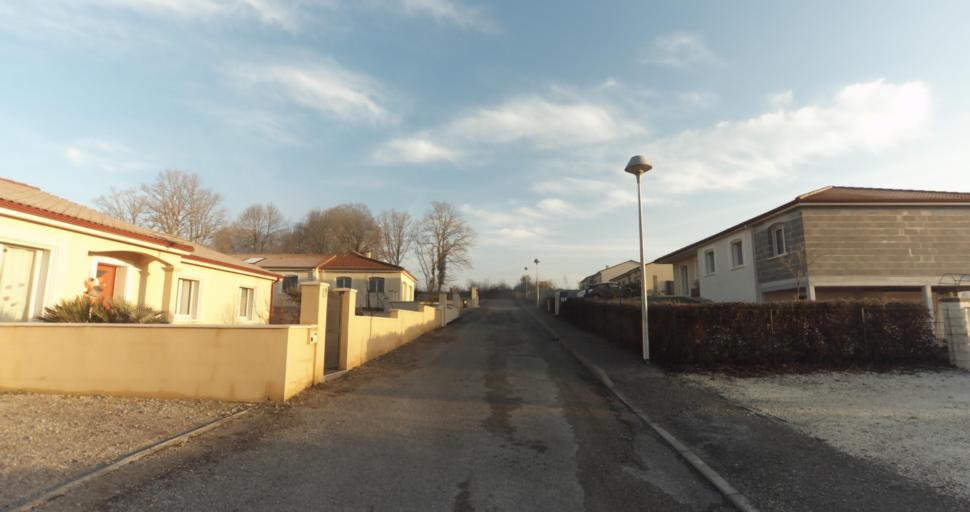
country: FR
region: Limousin
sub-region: Departement de la Haute-Vienne
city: Aixe-sur-Vienne
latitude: 45.7927
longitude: 1.1584
